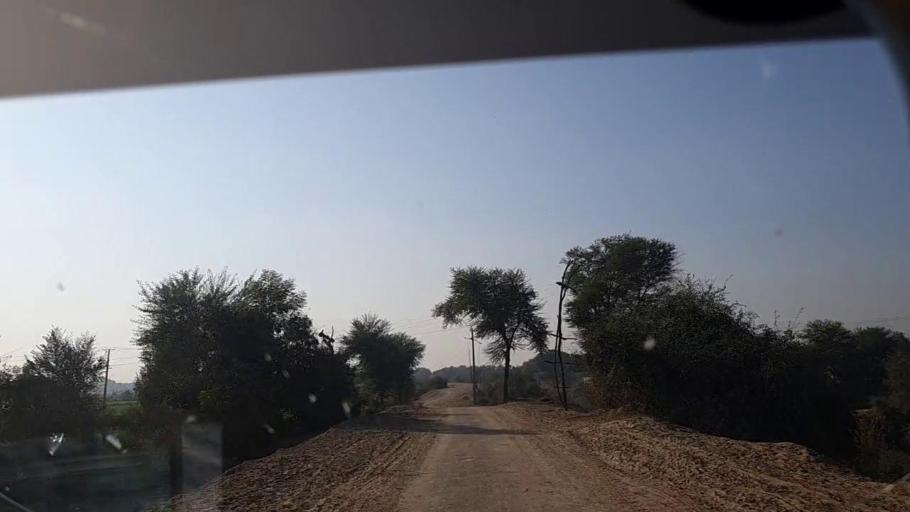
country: PK
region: Sindh
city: Sobhadero
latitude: 27.2338
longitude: 68.2683
